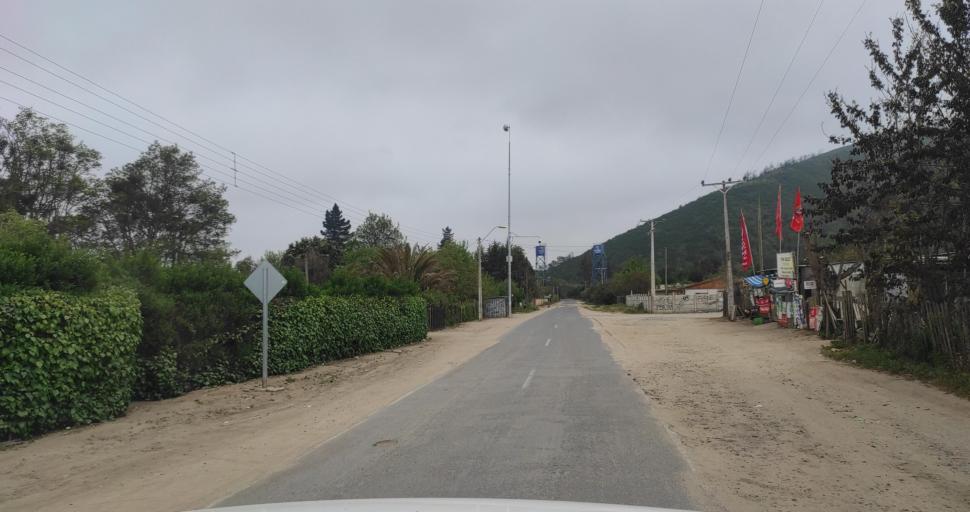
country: CL
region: Valparaiso
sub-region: Provincia de Marga Marga
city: Villa Alemana
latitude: -33.3589
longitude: -71.3021
